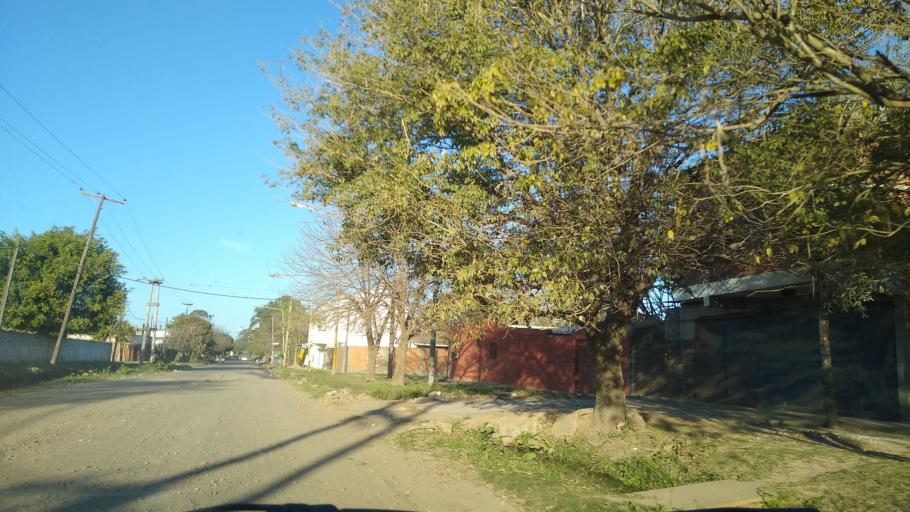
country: AR
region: Chaco
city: Barranqueras
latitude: -27.4800
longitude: -58.9474
